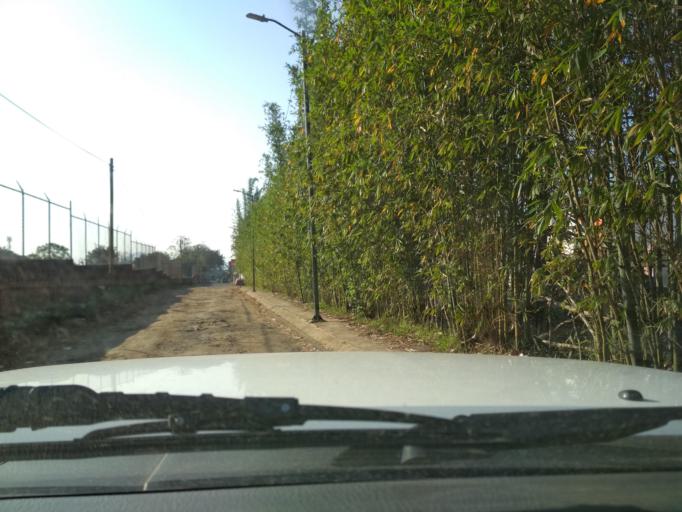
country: MX
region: Veracruz
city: Cordoba
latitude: 18.8703
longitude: -96.9311
